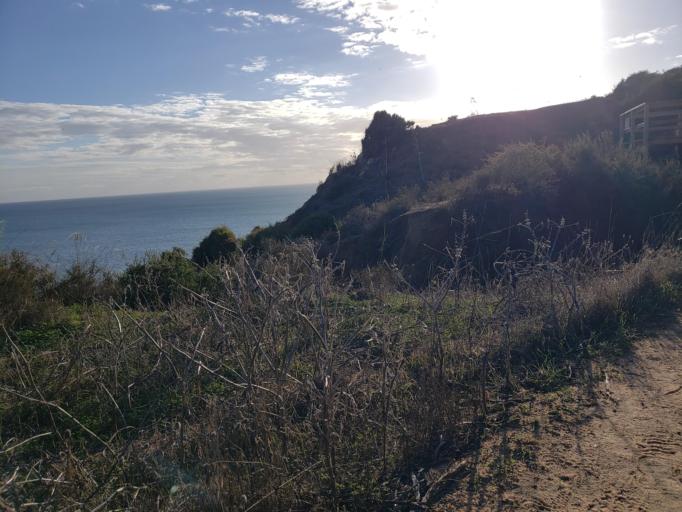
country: PT
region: Faro
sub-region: Lagos
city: Lagos
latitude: 37.0825
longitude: -8.6736
